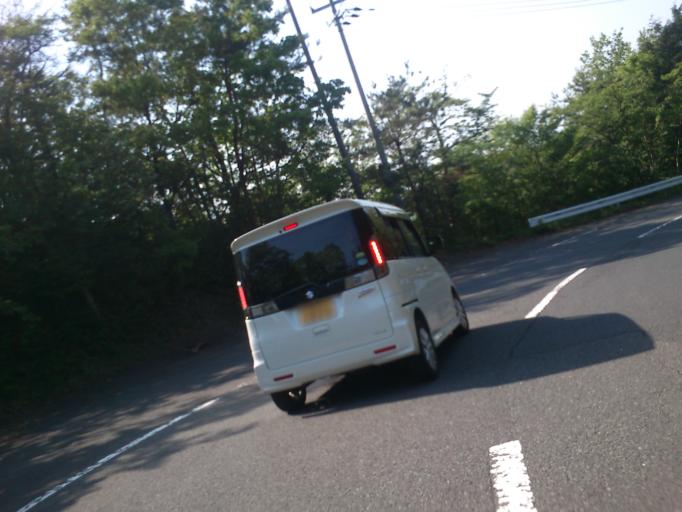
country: JP
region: Kyoto
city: Miyazu
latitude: 35.7415
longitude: 135.1732
